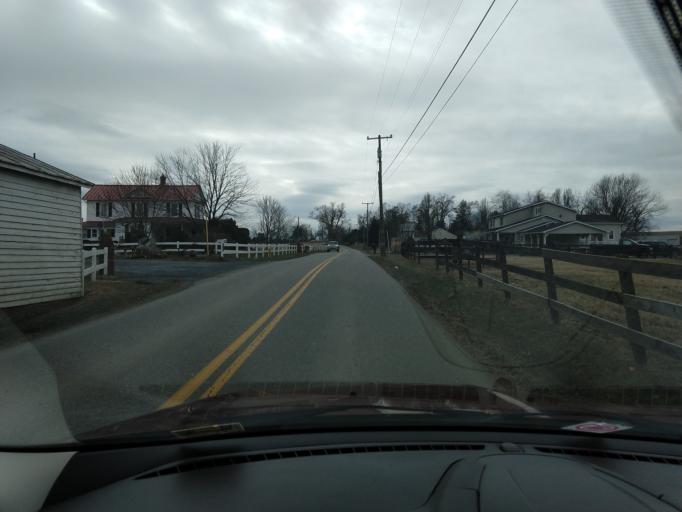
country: US
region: Virginia
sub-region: Augusta County
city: Crimora
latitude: 38.1942
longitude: -78.9090
